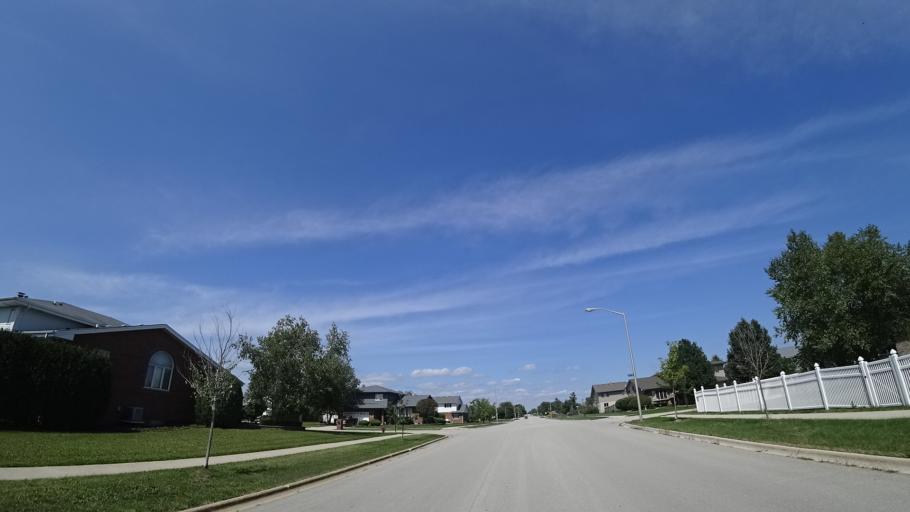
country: US
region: Illinois
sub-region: Cook County
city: Orland Hills
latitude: 41.5700
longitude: -87.8322
